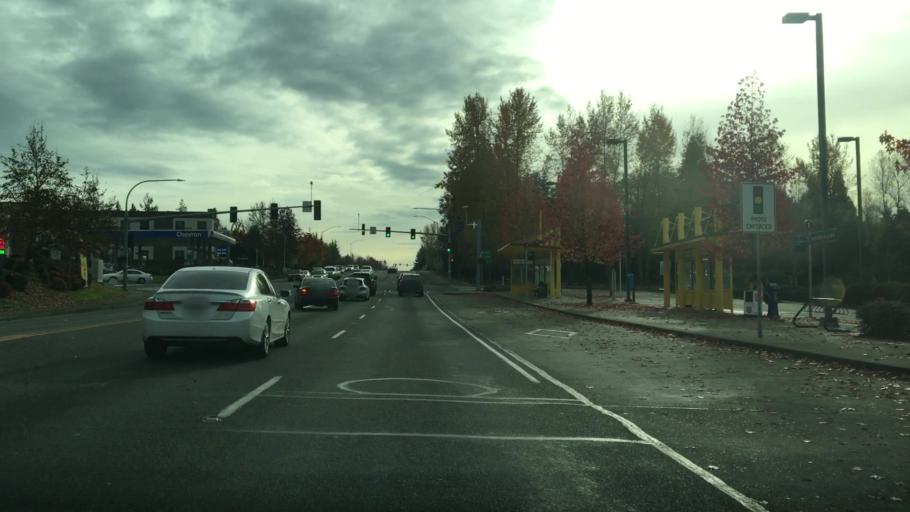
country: US
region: Washington
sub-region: Pierce County
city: Puyallup
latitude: 47.1616
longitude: -122.3042
